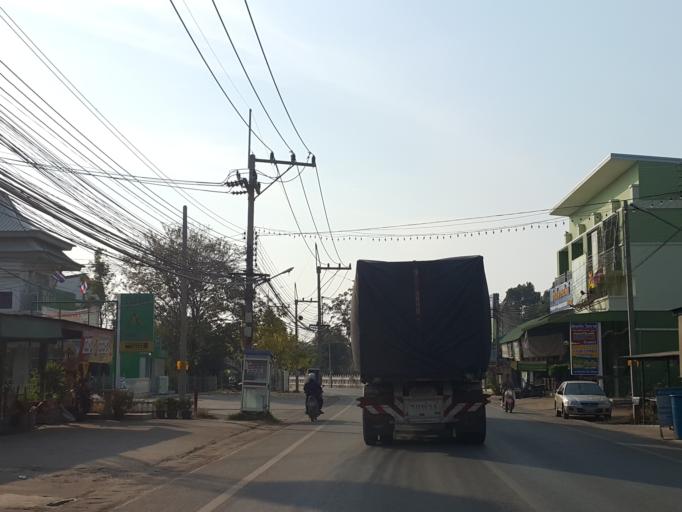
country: TH
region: Phitsanulok
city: Phrom Phiram
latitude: 17.0363
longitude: 100.1980
